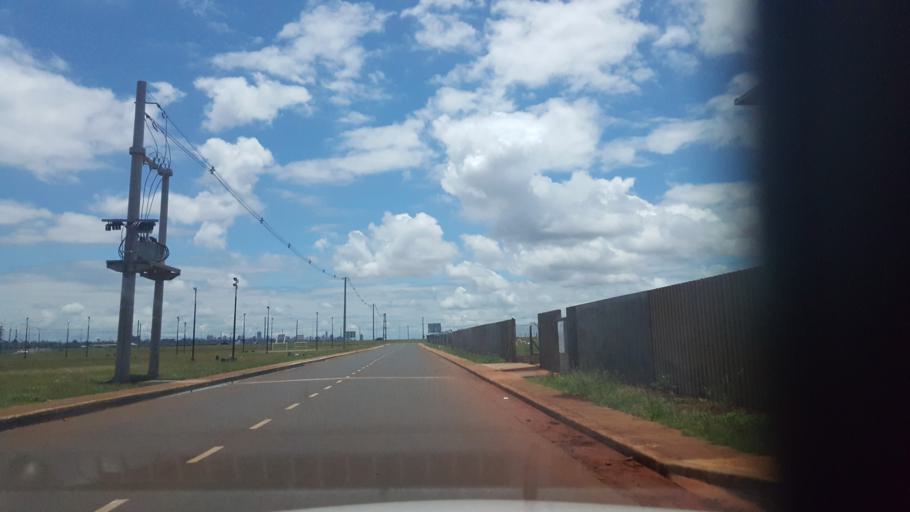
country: AR
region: Misiones
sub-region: Departamento de Capital
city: Posadas
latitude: -27.4184
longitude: -55.8860
